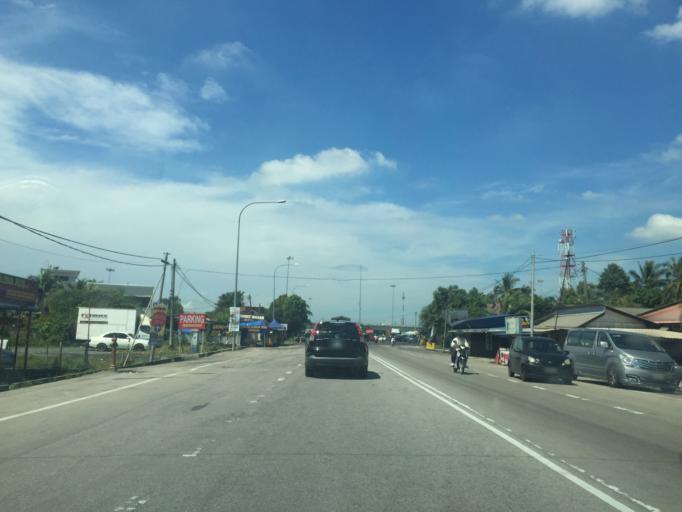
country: MY
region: Penang
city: Permatang Kuching
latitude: 5.4464
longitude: 100.4216
